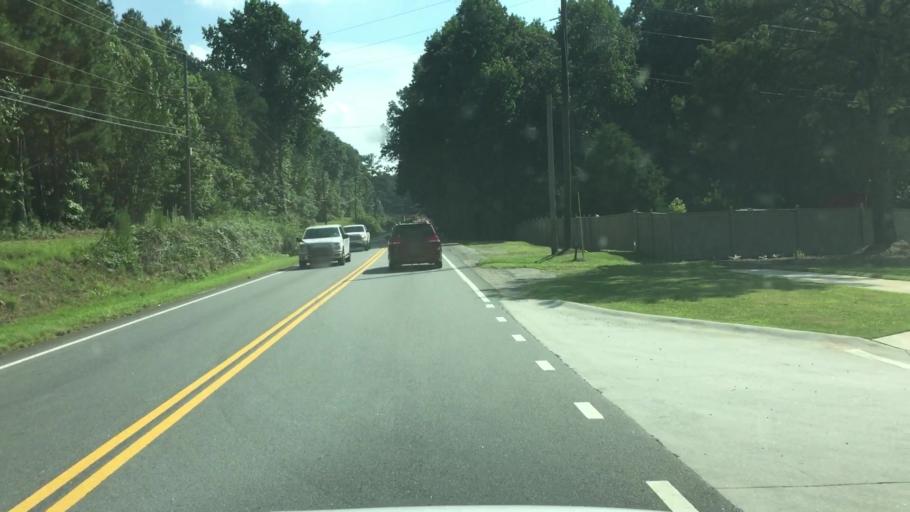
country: US
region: Georgia
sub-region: Gwinnett County
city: Dacula
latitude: 33.9951
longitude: -83.8821
